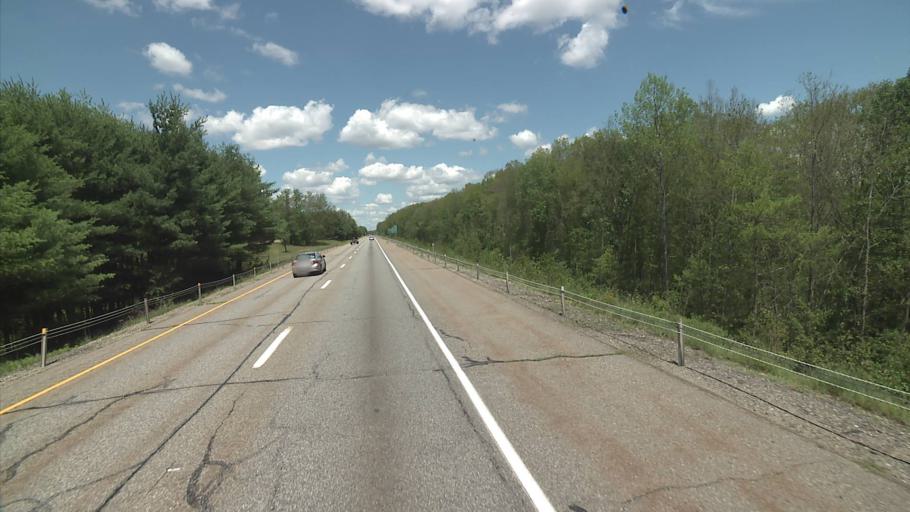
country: US
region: Connecticut
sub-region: Windham County
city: Thompson
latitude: 41.9890
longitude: -71.8527
